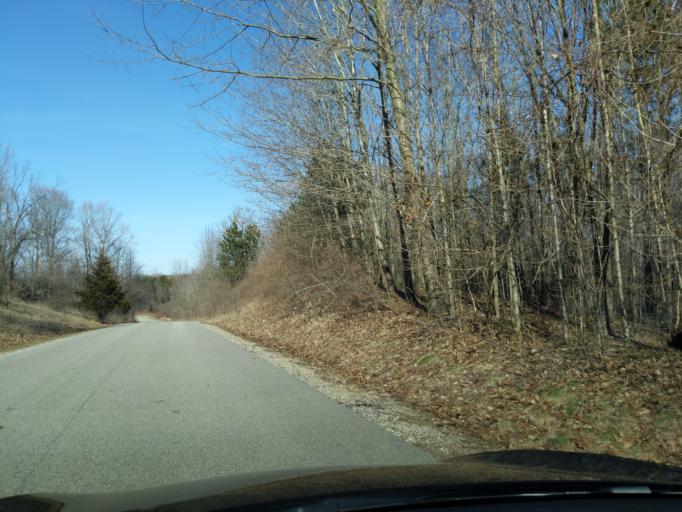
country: US
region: Michigan
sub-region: Ionia County
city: Saranac
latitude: 42.9395
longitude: -85.1363
